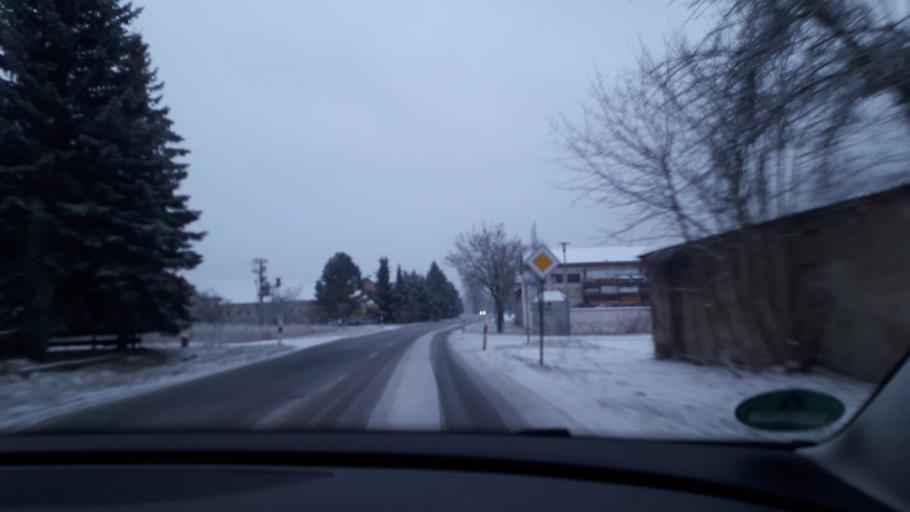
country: DE
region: Brandenburg
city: Spremberg
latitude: 51.5987
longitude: 14.4520
